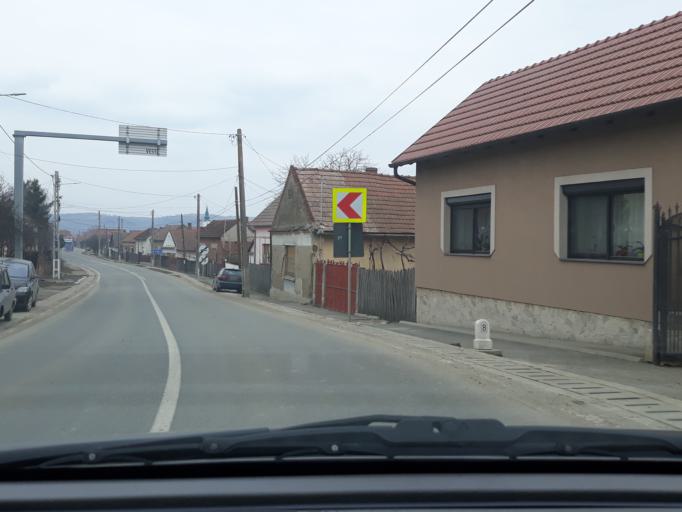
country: RO
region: Salaj
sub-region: Comuna Nusfalau
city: Nusfalau
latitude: 47.1903
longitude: 22.7015
